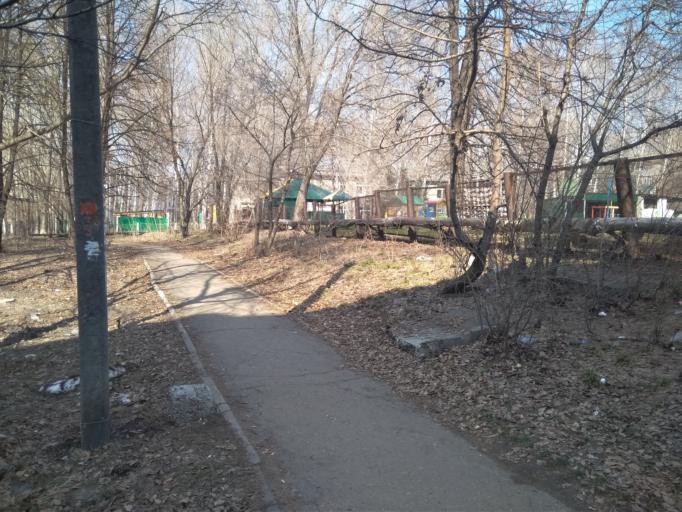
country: RU
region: Ulyanovsk
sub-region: Ulyanovskiy Rayon
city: Ulyanovsk
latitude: 54.2593
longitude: 48.3311
